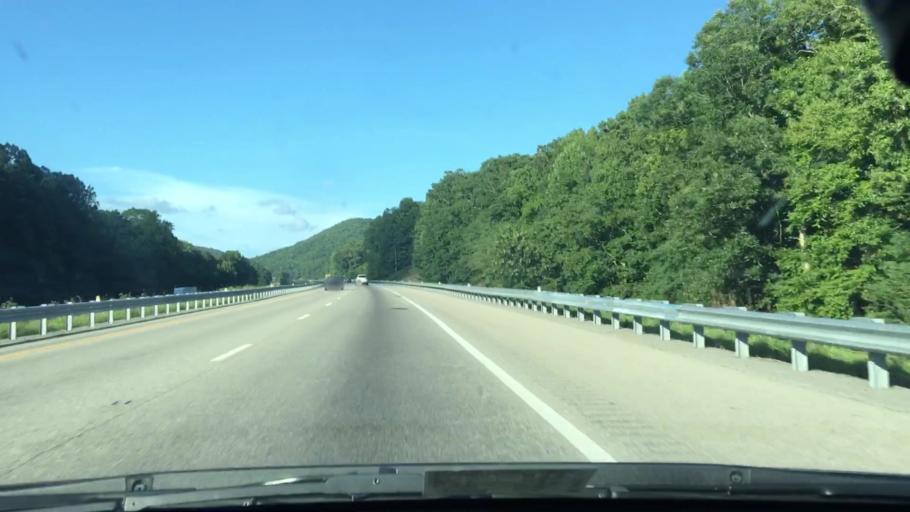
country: US
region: Virginia
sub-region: Alleghany County
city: Clifton Forge
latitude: 37.8394
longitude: -79.6416
